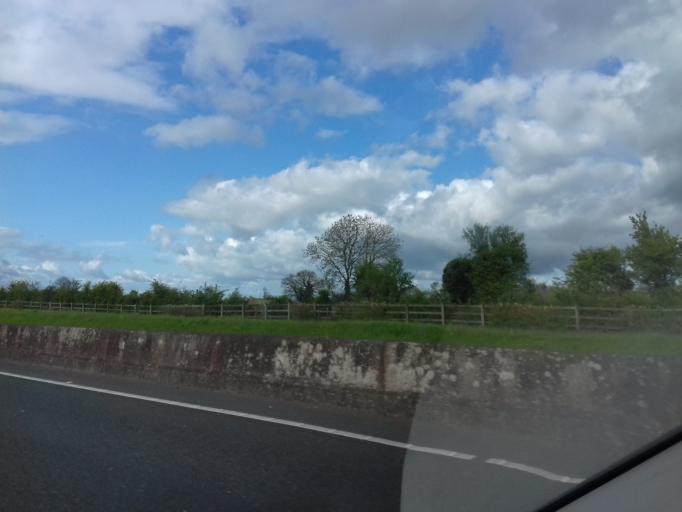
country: IE
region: Leinster
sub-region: Kilkenny
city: Thomastown
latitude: 52.4752
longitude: -7.2398
